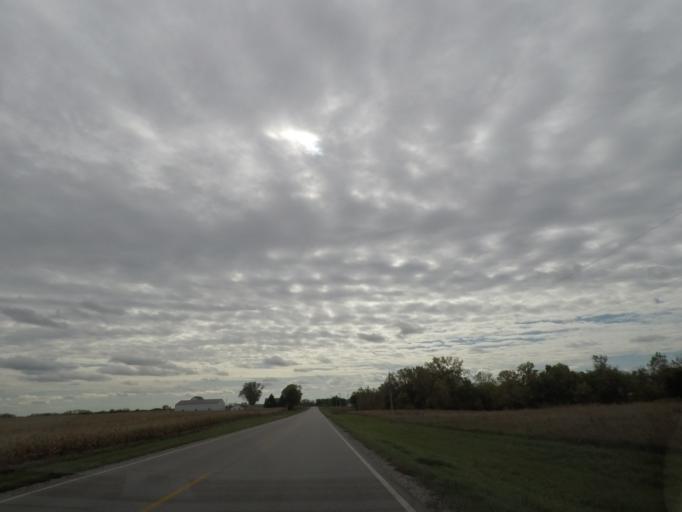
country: US
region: Iowa
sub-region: Story County
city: Huxley
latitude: 41.8455
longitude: -93.5316
